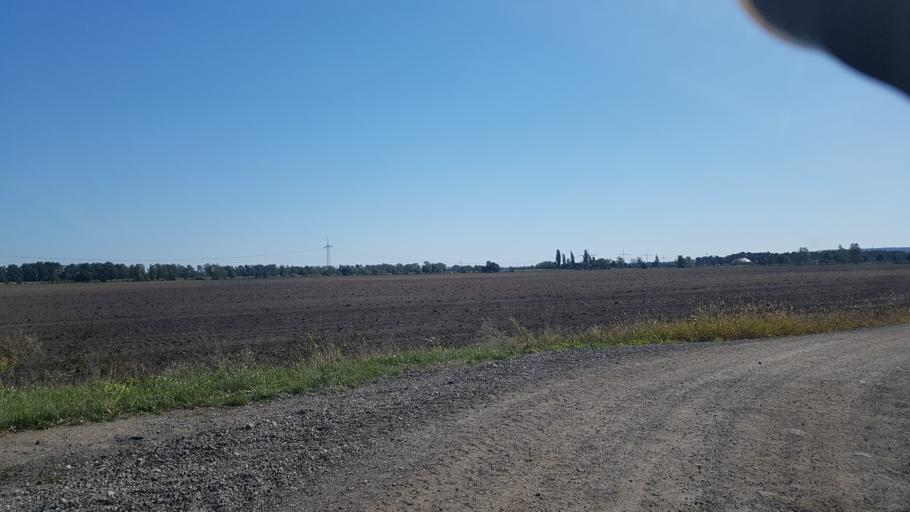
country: DE
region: Brandenburg
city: Elsterwerda
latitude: 51.4493
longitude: 13.5410
